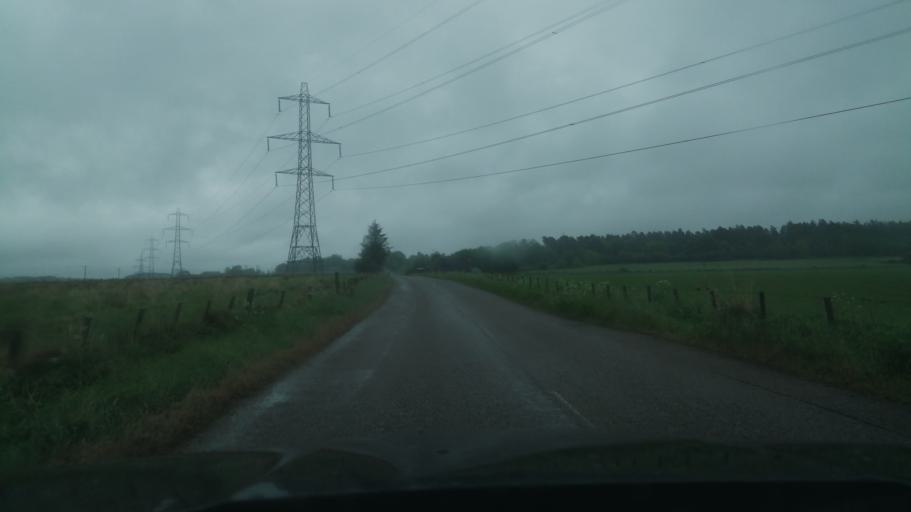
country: GB
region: Scotland
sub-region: Aberdeenshire
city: Huntly
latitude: 57.5449
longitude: -2.8082
